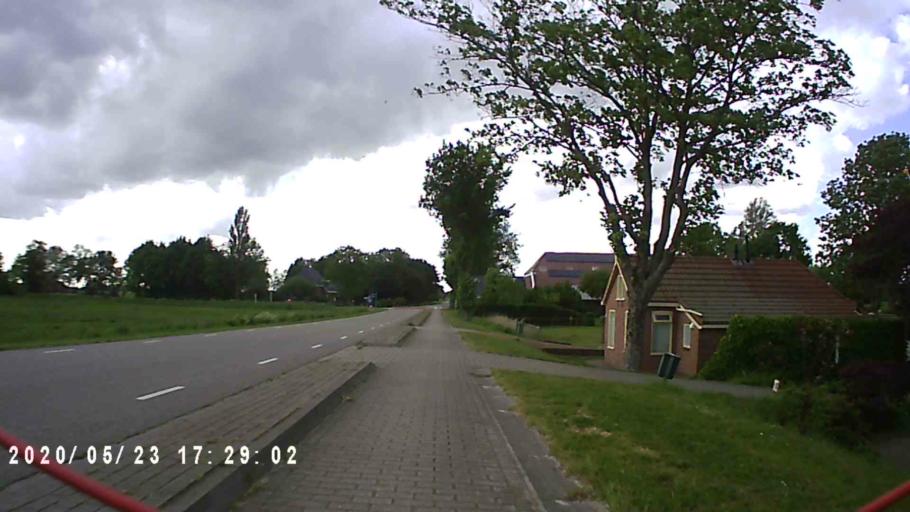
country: NL
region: Groningen
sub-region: Gemeente Slochteren
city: Slochteren
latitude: 53.2592
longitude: 6.7791
